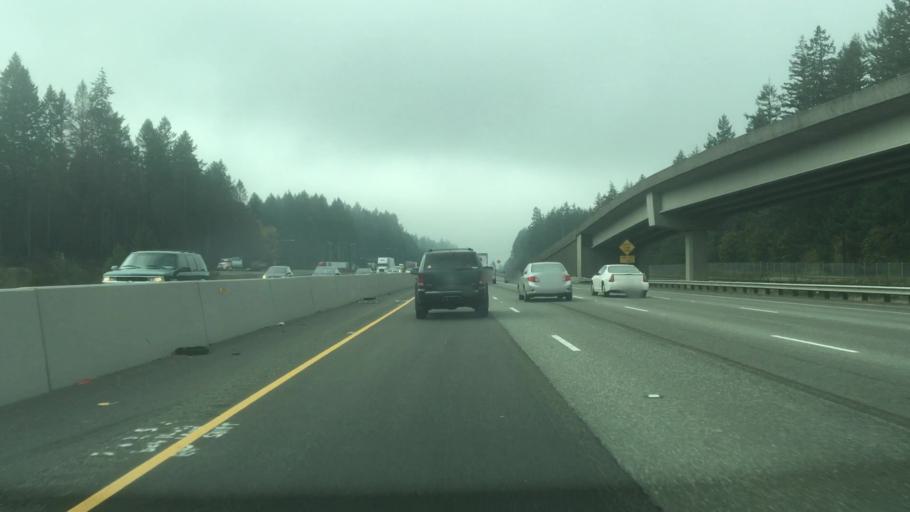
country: US
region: Washington
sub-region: Pierce County
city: DuPont
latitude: 47.0872
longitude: -122.6480
